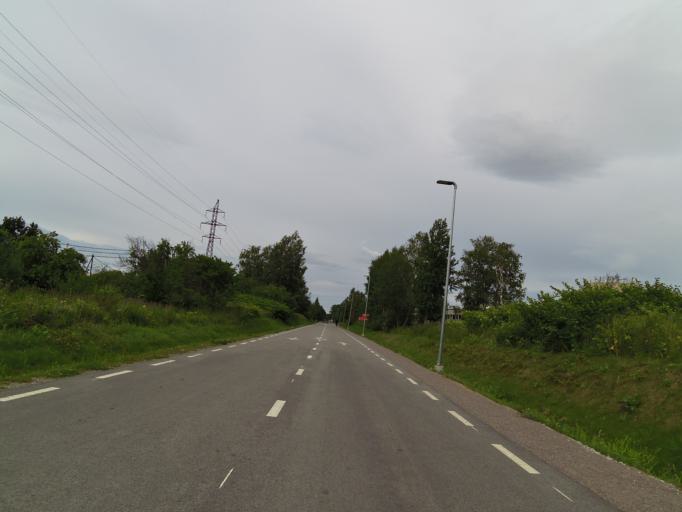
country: EE
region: Harju
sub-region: Tallinna linn
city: Tallinn
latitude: 59.4207
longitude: 24.6753
